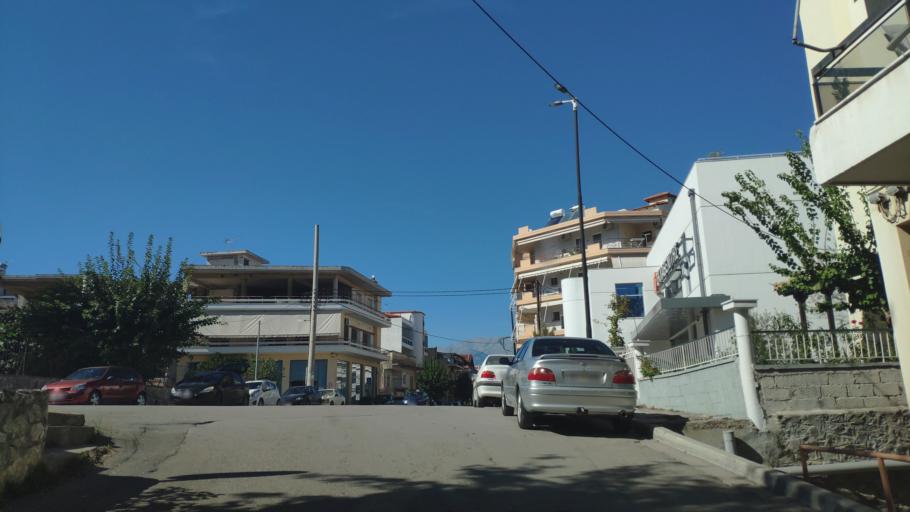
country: GR
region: Central Greece
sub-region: Nomos Voiotias
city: Livadeia
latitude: 38.4392
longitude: 22.8711
